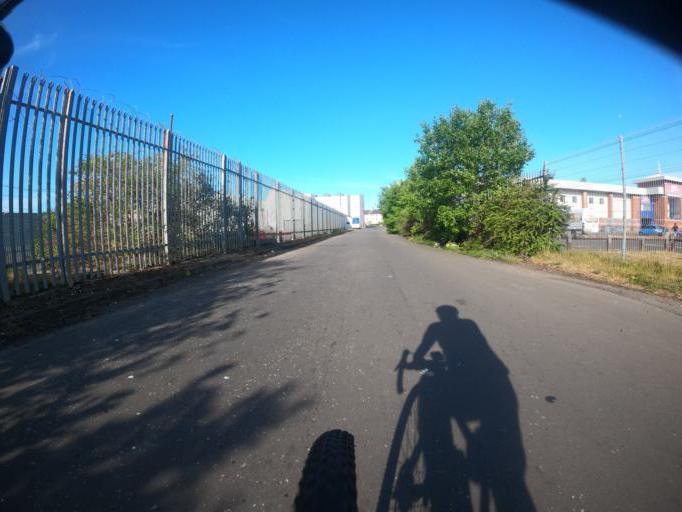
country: GB
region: Scotland
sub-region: Edinburgh
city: Edinburgh
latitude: 55.9794
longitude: -3.2337
